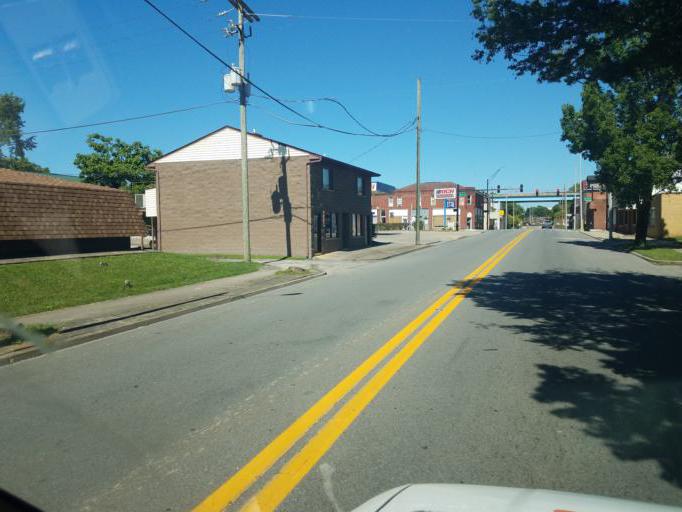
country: US
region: West Virginia
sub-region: Cabell County
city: Huntington
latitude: 38.4297
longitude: -82.3876
